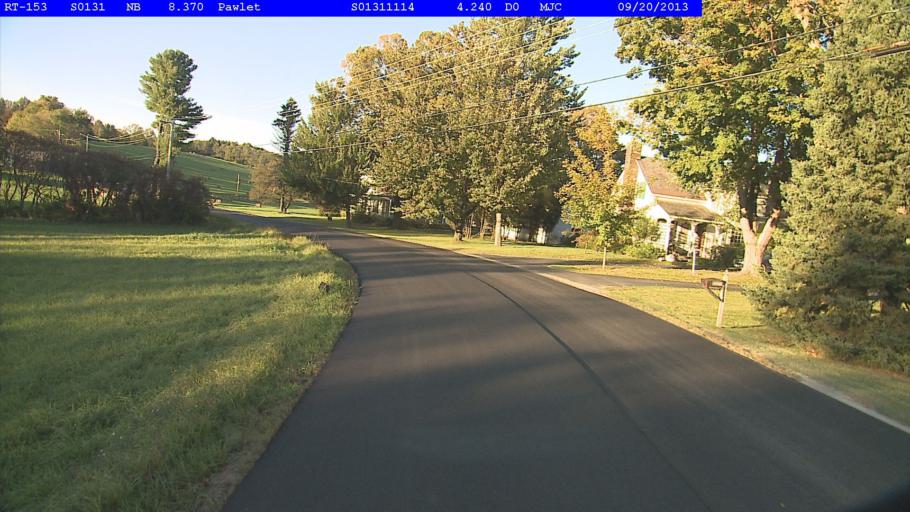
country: US
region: New York
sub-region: Washington County
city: Granville
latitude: 43.3676
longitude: -73.2346
